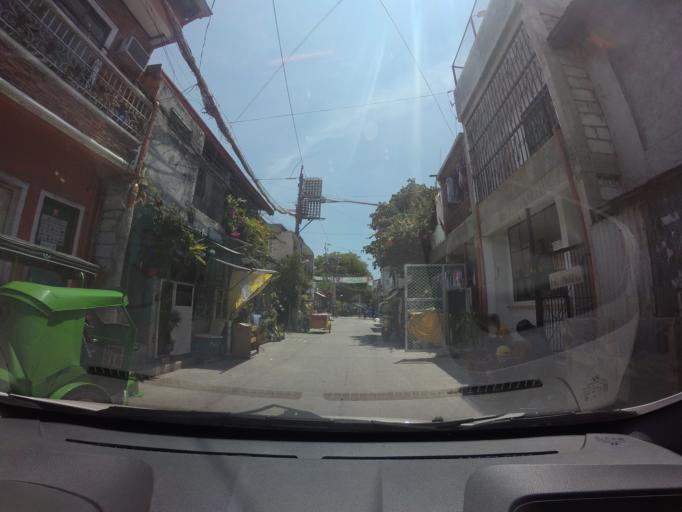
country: PH
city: Sambayanihan People's Village
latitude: 14.4226
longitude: 121.0093
